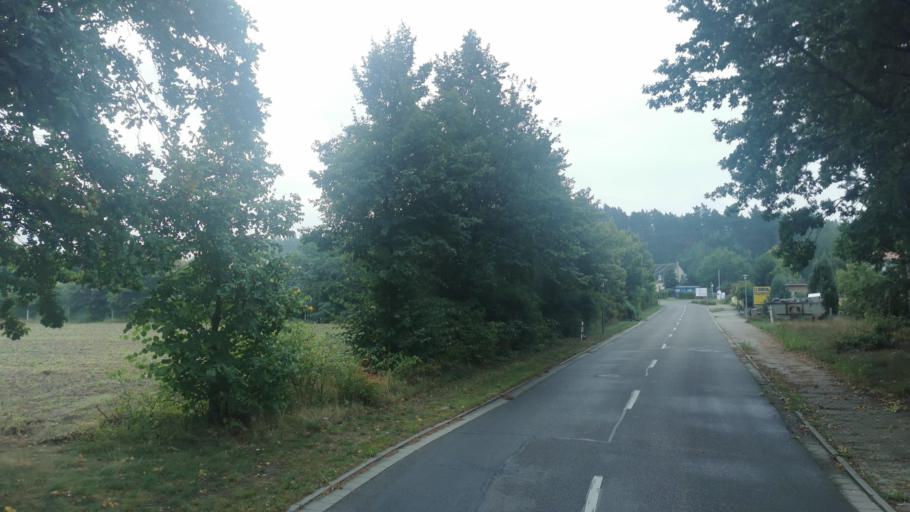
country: DE
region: Brandenburg
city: Kolkwitz
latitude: 51.7388
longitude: 14.2525
